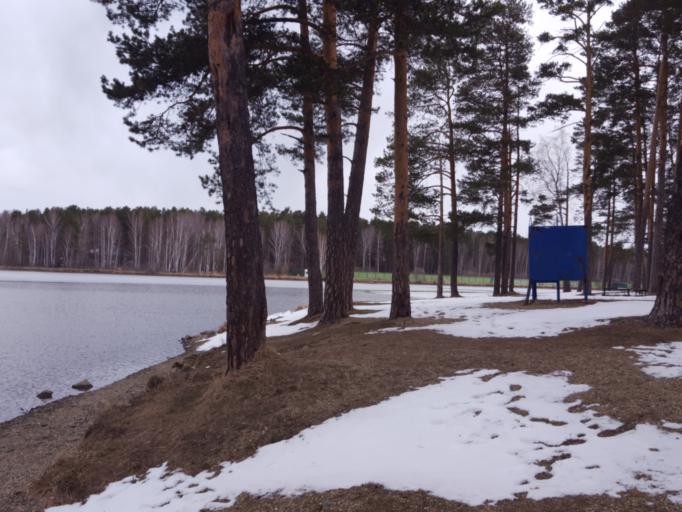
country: RU
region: Sverdlovsk
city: Istok
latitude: 56.7773
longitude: 60.8107
